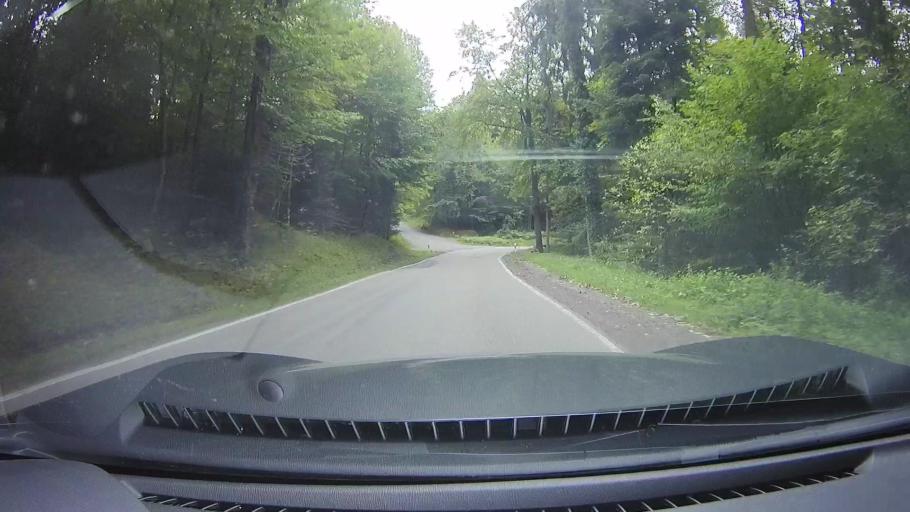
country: DE
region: Baden-Wuerttemberg
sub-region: Regierungsbezirk Stuttgart
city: Althutte
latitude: 48.9410
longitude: 9.5584
